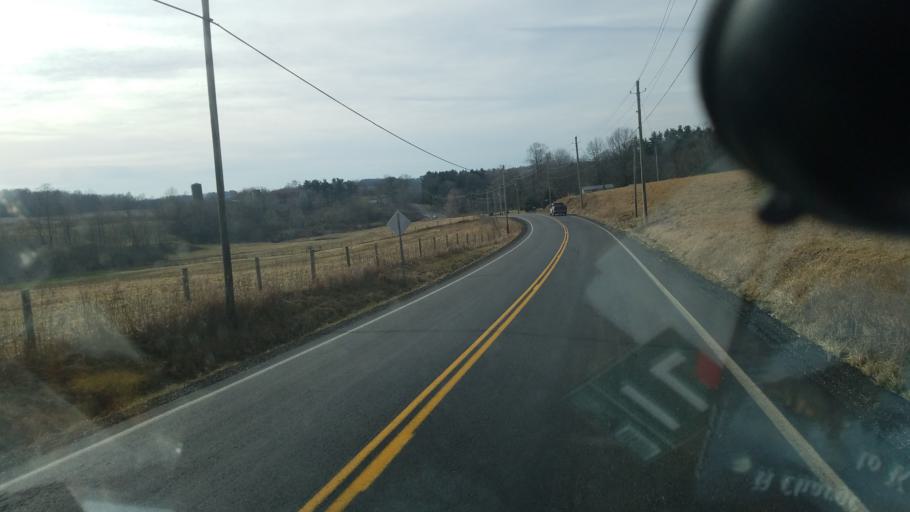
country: US
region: Ohio
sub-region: Holmes County
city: Millersburg
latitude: 40.6113
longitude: -81.8323
